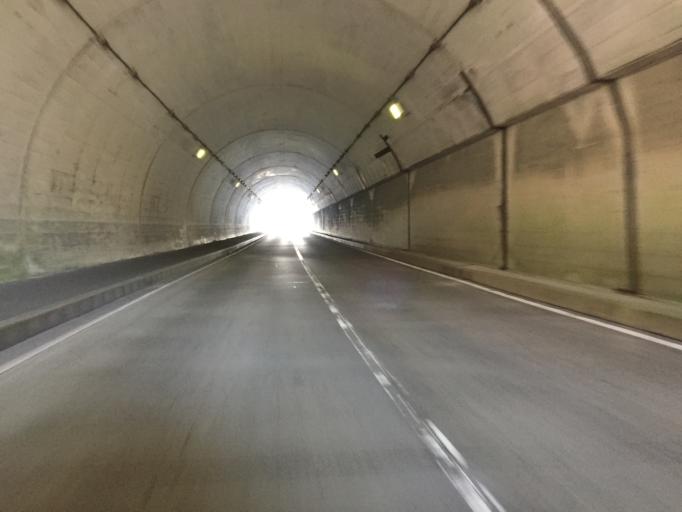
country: JP
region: Fukushima
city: Iwaki
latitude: 36.9441
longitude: 140.9169
